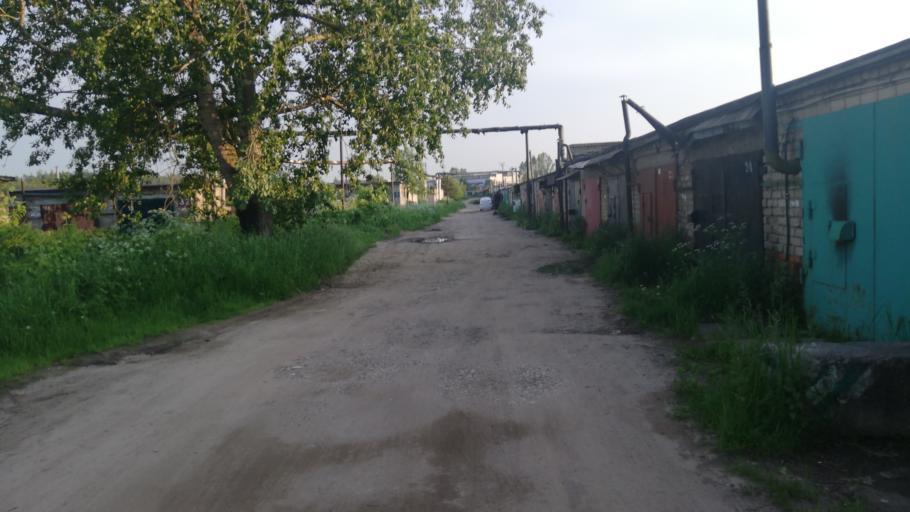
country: RU
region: Jaroslavl
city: Yaroslavl
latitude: 57.5765
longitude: 39.8363
